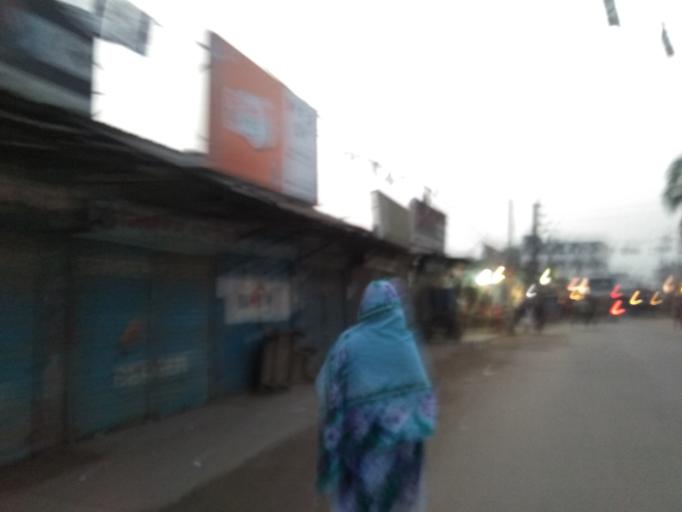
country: BD
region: Rangpur Division
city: Rangpur
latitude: 25.7408
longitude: 89.2506
